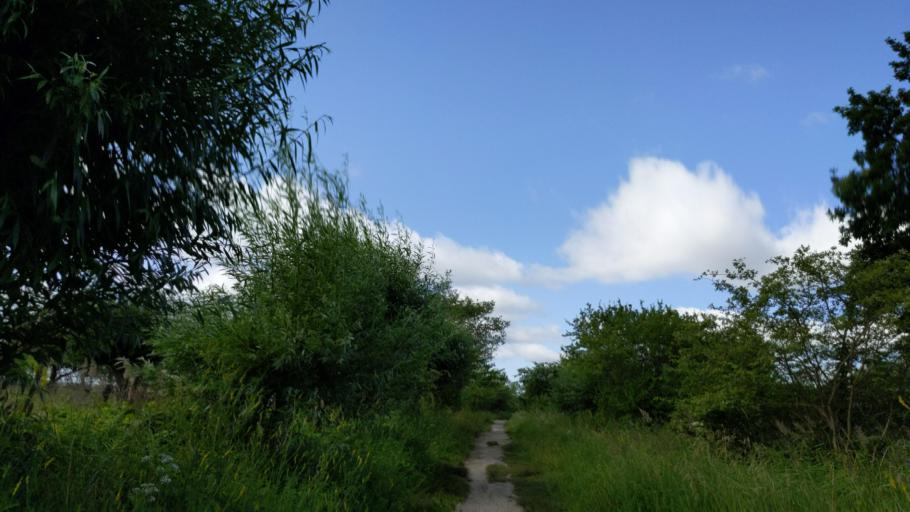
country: DE
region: Schleswig-Holstein
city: Travemuende
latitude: 53.9433
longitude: 10.8712
